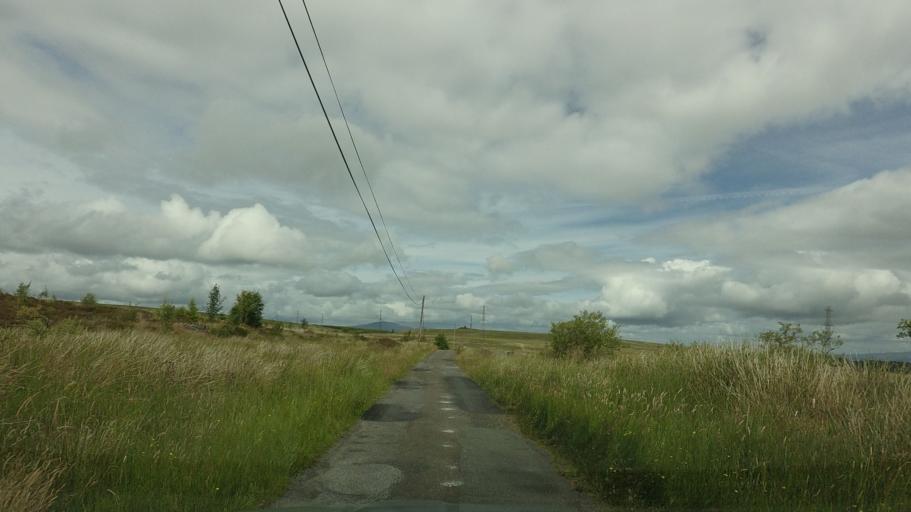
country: GB
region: Scotland
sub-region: Stirling
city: Killearn
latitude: 56.0897
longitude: -4.4339
